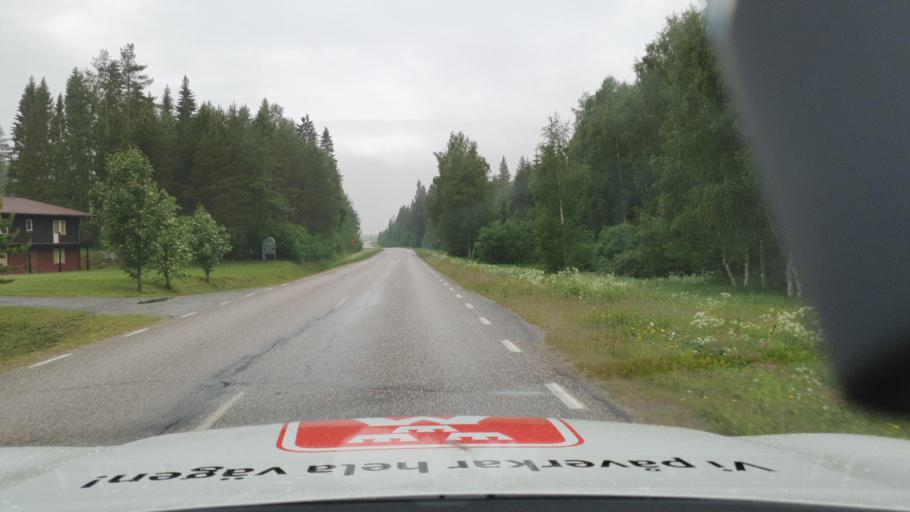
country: SE
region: Vaesterbotten
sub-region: Vannas Kommun
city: Vaennaes
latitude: 63.7720
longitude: 19.6144
